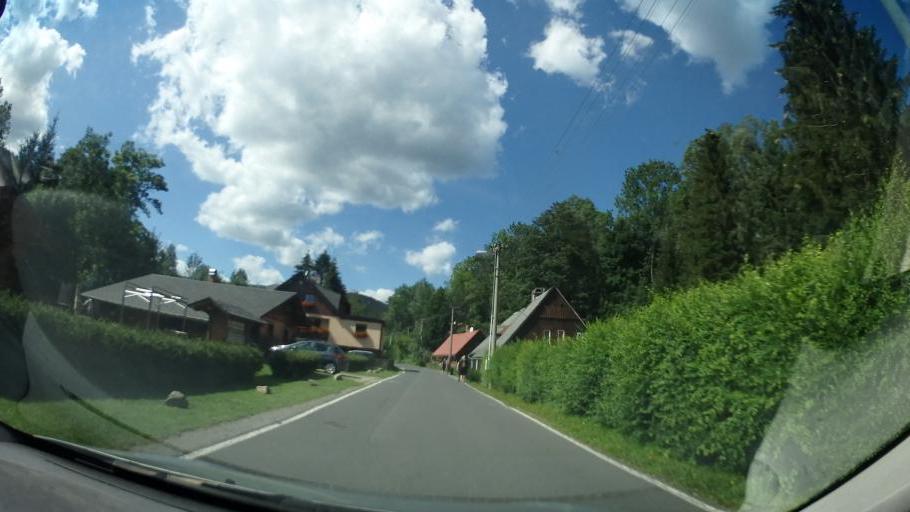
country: CZ
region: Olomoucky
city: Vapenna
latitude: 50.2252
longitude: 17.0908
